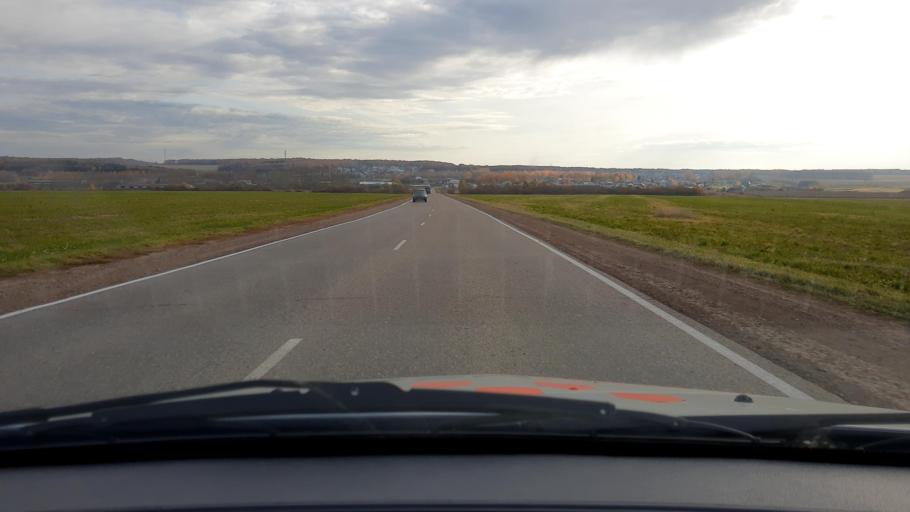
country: RU
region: Bashkortostan
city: Avdon
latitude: 54.8218
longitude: 55.6685
